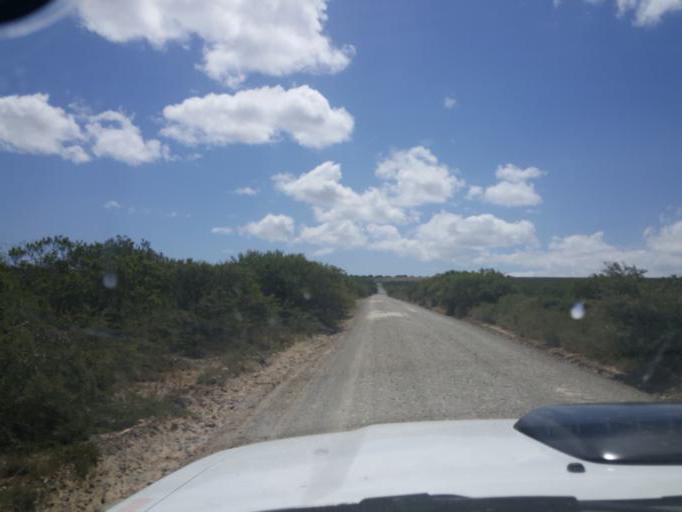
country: ZA
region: Eastern Cape
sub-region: Cacadu District Municipality
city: Grahamstown
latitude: -33.5443
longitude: 26.1042
